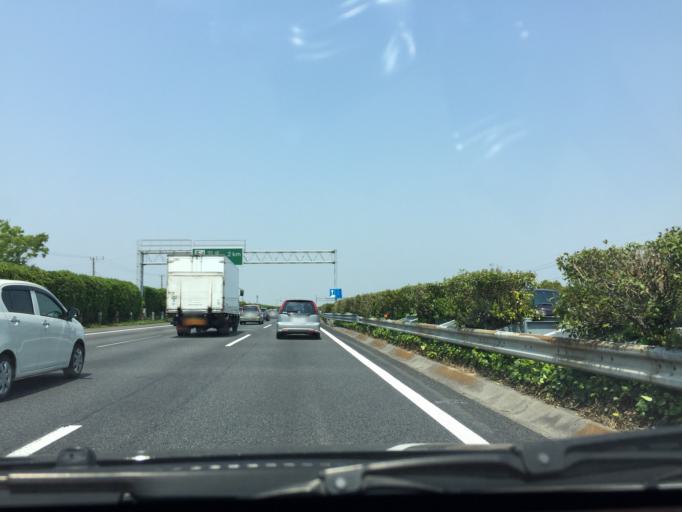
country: JP
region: Saitama
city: Kazo
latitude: 36.1501
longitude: 139.5990
